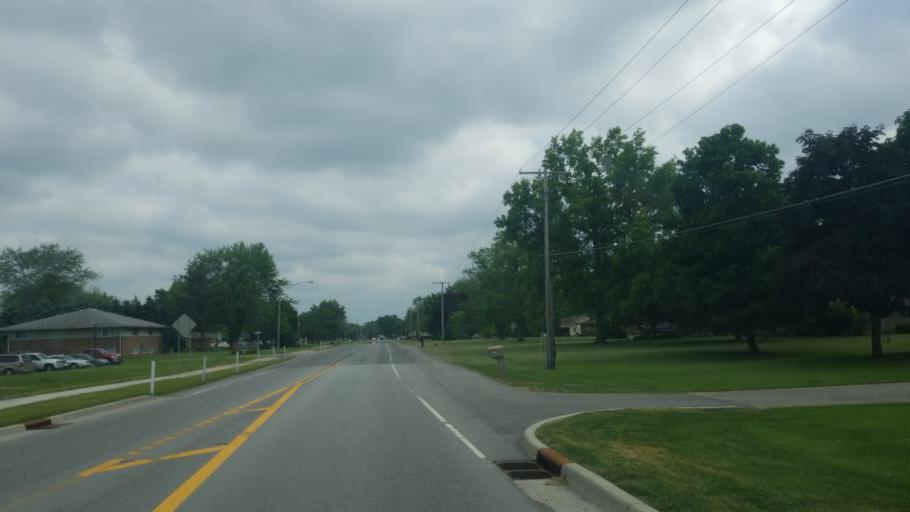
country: US
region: Indiana
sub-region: Elkhart County
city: Nappanee
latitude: 41.4563
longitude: -86.0015
